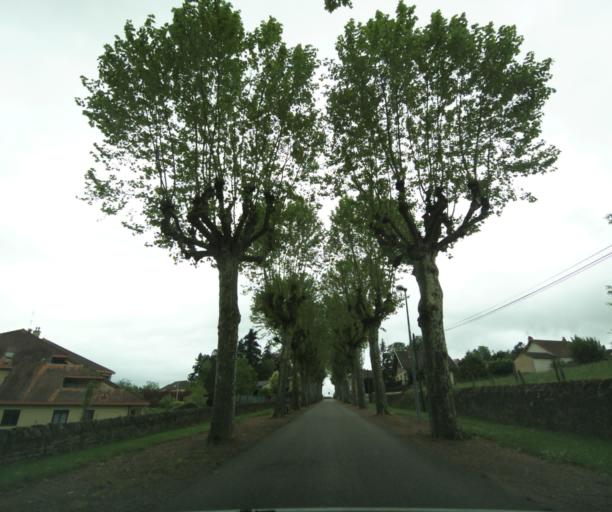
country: FR
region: Bourgogne
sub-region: Departement de Saone-et-Loire
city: Charolles
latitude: 46.4396
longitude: 4.2721
